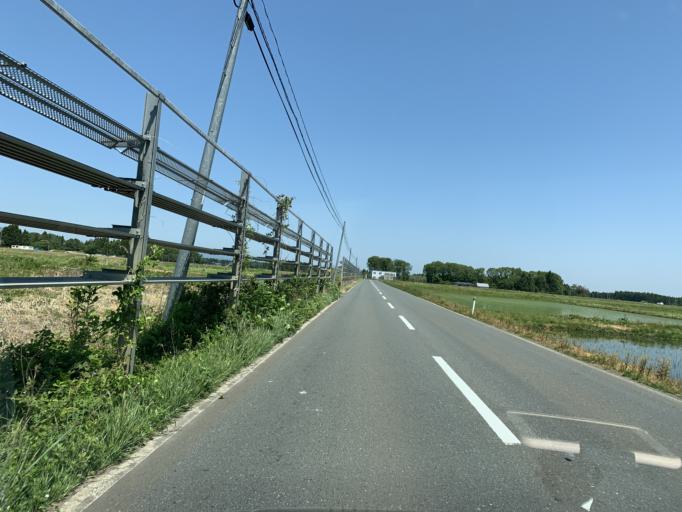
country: JP
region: Iwate
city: Kitakami
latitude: 39.2566
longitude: 141.0646
